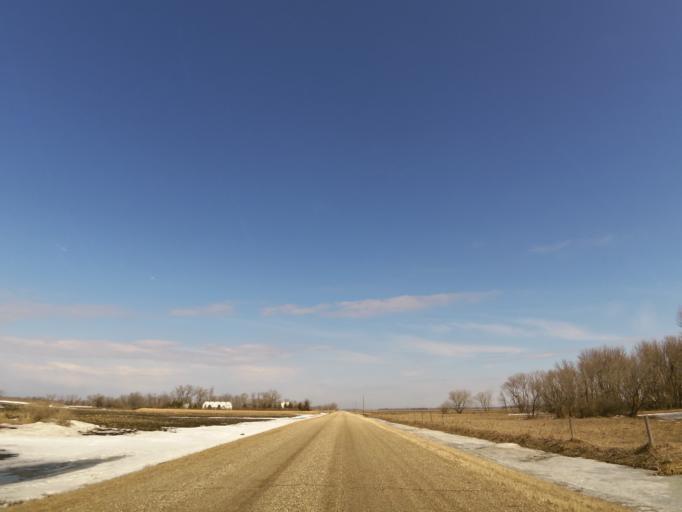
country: US
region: North Dakota
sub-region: Walsh County
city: Grafton
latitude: 48.3918
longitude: -97.1684
